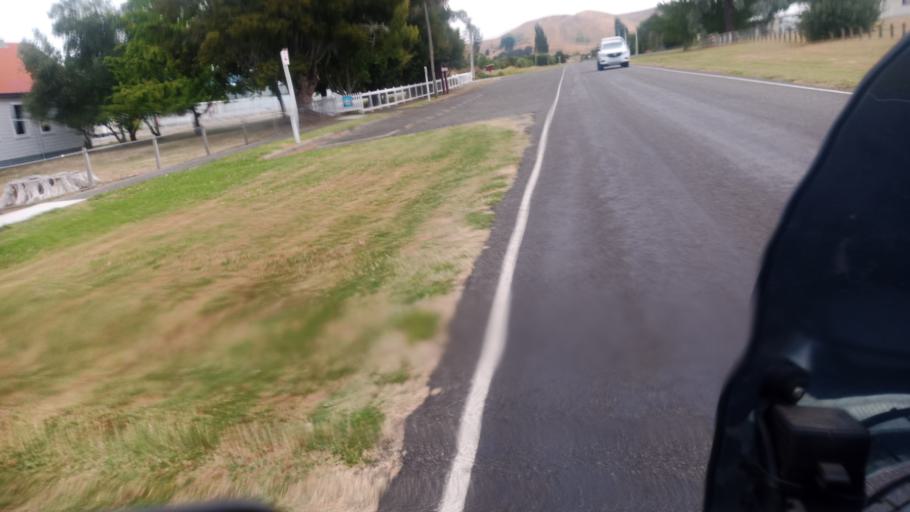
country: NZ
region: Gisborne
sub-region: Gisborne District
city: Gisborne
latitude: -38.6258
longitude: 177.8888
